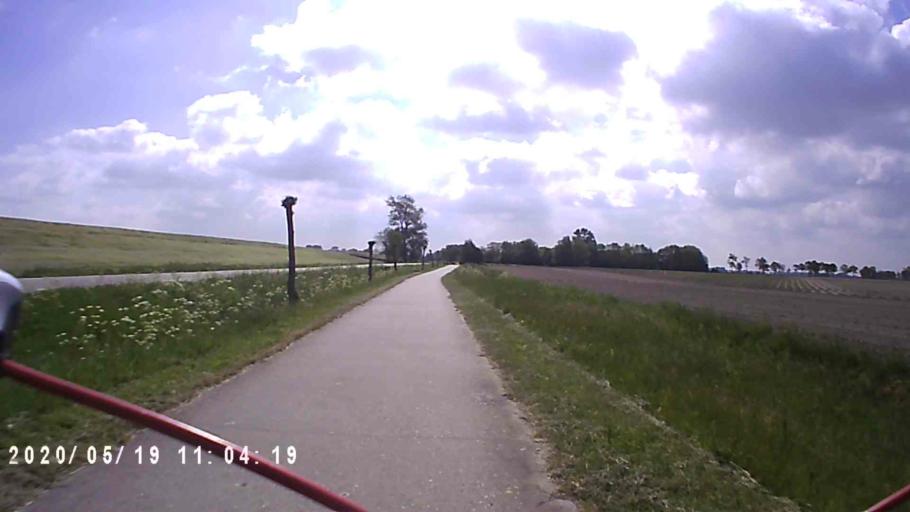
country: NL
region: Groningen
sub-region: Gemeente Zuidhorn
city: Grijpskerk
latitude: 53.2974
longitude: 6.2843
